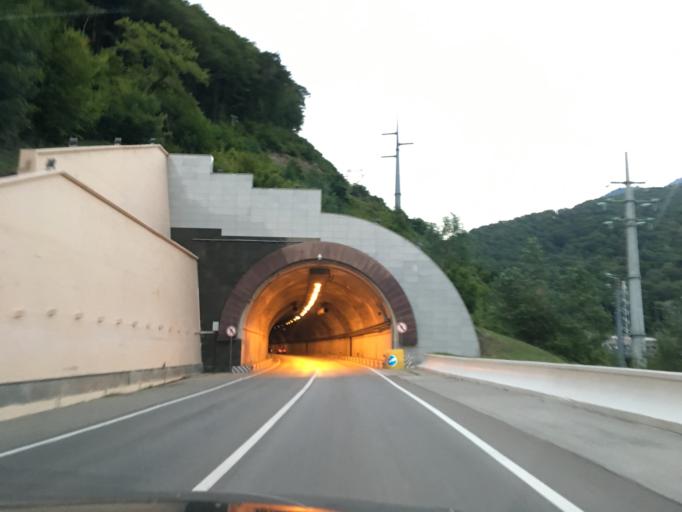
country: RU
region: Krasnodarskiy
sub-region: Sochi City
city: Krasnaya Polyana
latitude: 43.6513
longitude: 40.1499
